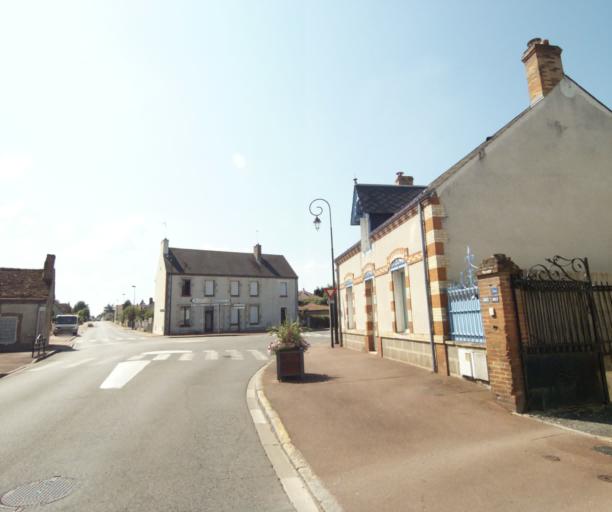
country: FR
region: Centre
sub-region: Departement du Loiret
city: Saint-Cyr-en-Val
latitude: 47.8302
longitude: 1.9699
